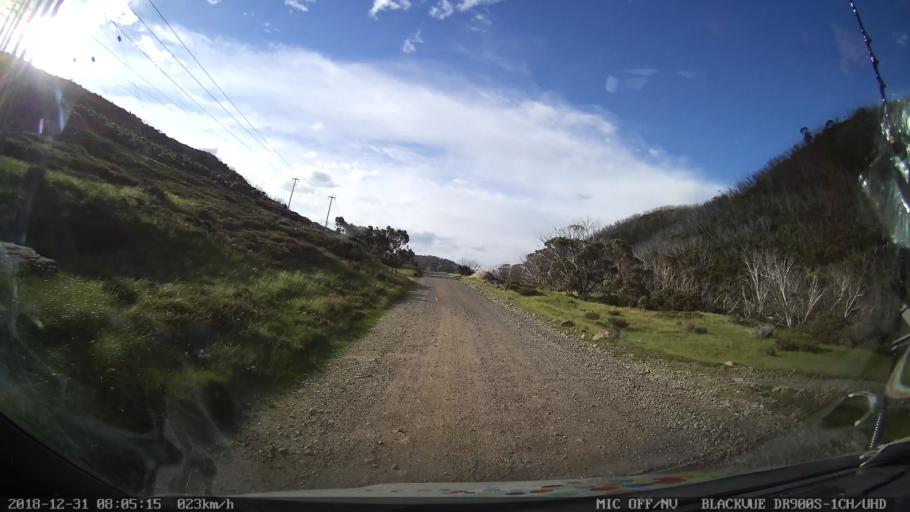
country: AU
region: New South Wales
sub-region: Snowy River
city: Jindabyne
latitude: -36.3704
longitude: 148.4063
